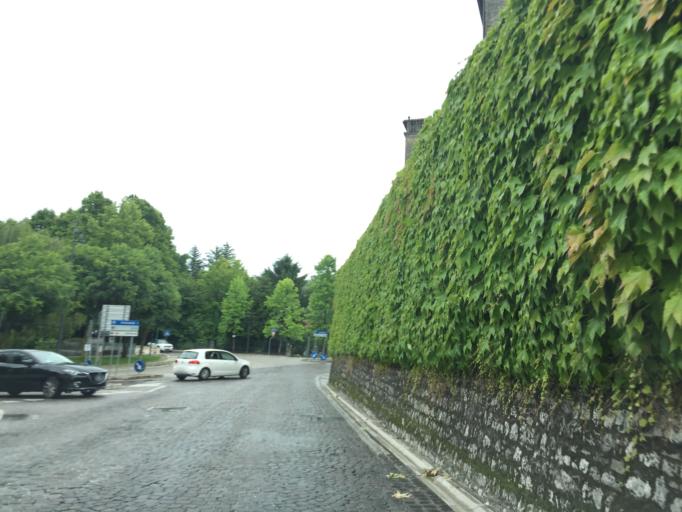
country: IT
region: Friuli Venezia Giulia
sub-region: Provincia di Pordenone
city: Porcia
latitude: 45.9582
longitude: 12.6151
